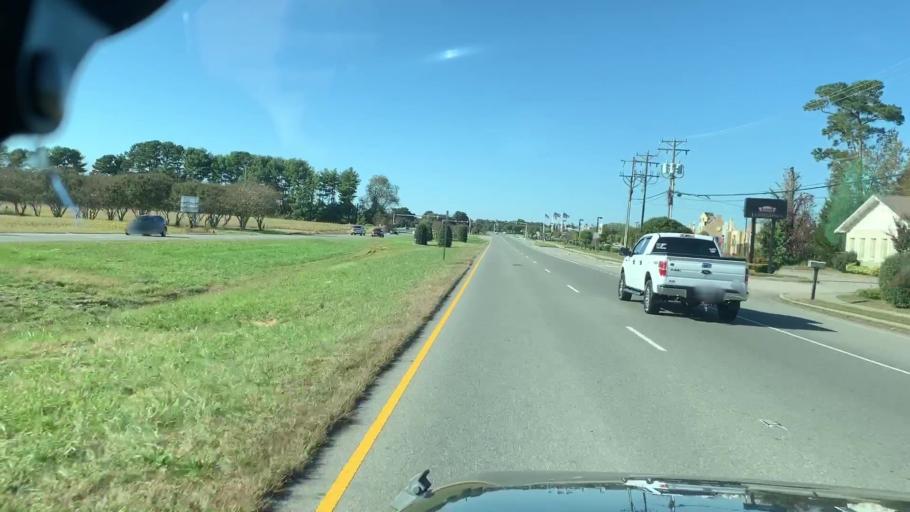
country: US
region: Virginia
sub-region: James City County
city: Williamsburg
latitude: 37.3465
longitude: -76.7591
